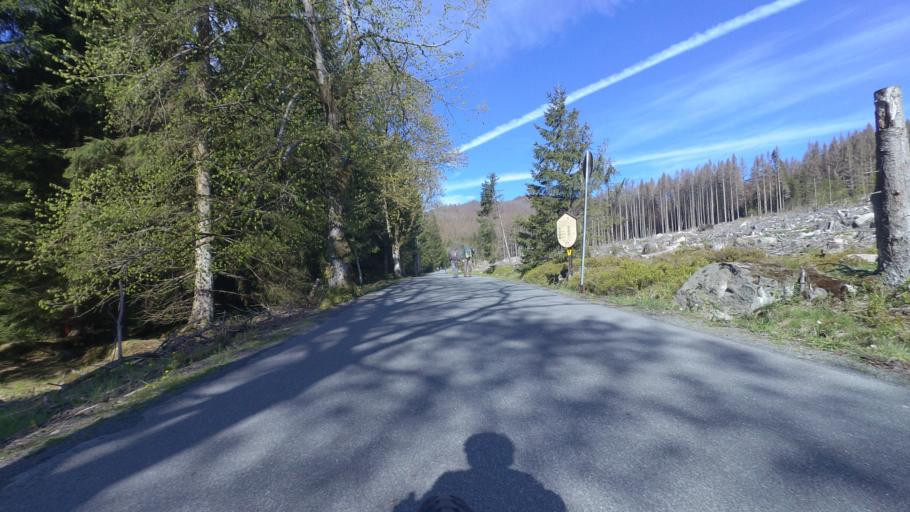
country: DE
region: Lower Saxony
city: Braunlage
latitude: 51.7727
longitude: 10.6414
